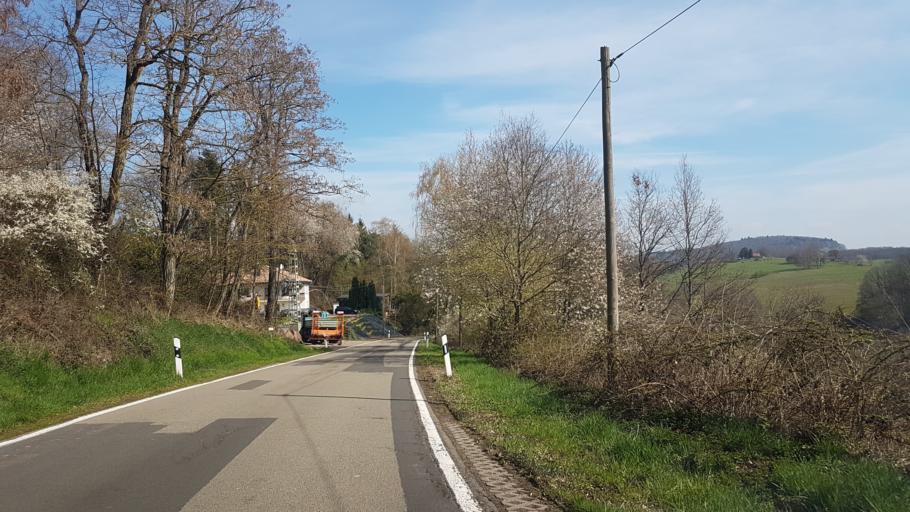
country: DE
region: Rheinland-Pfalz
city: Borsborn
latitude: 49.4343
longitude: 7.3921
